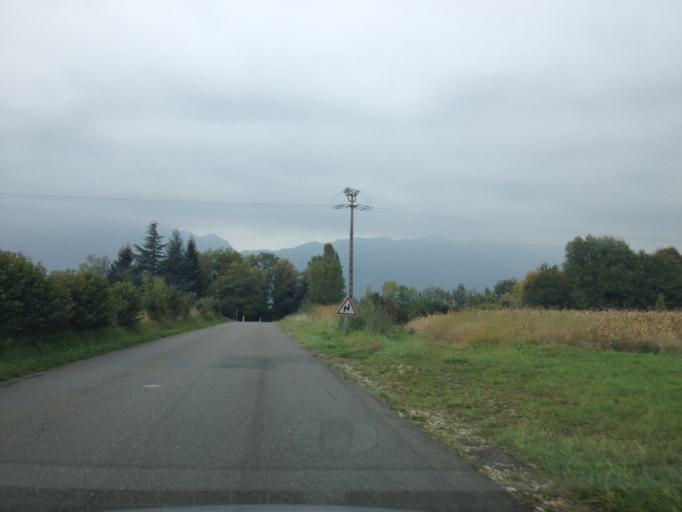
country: FR
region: Rhone-Alpes
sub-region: Departement de la Savoie
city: Mouxy
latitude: 45.6964
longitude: 5.9373
